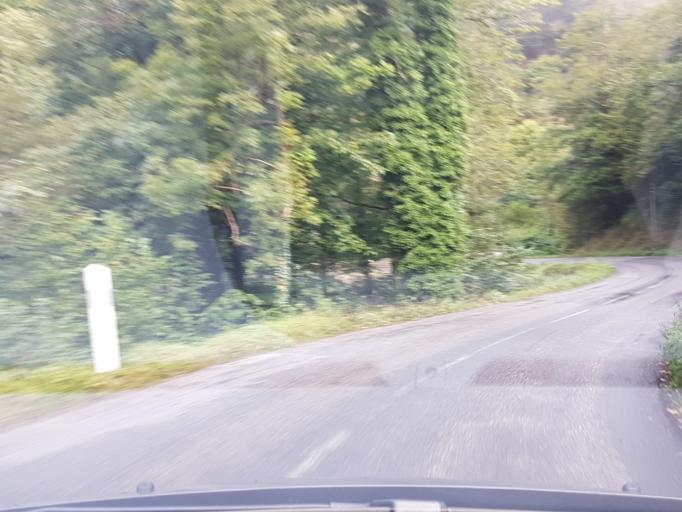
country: FR
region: Midi-Pyrenees
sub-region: Departement de l'Ariege
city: Montjoie-en-Couserans
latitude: 42.9071
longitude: 1.3712
